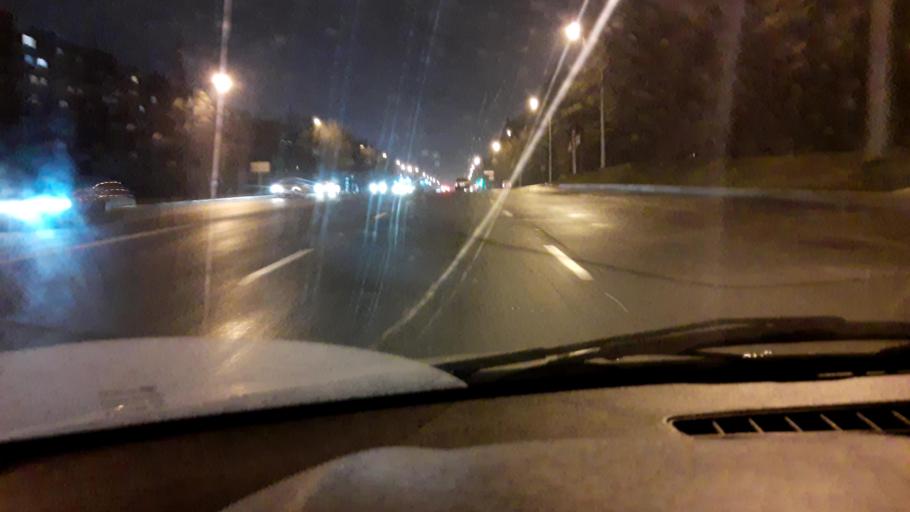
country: RU
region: Bashkortostan
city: Ufa
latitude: 54.7374
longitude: 56.0275
